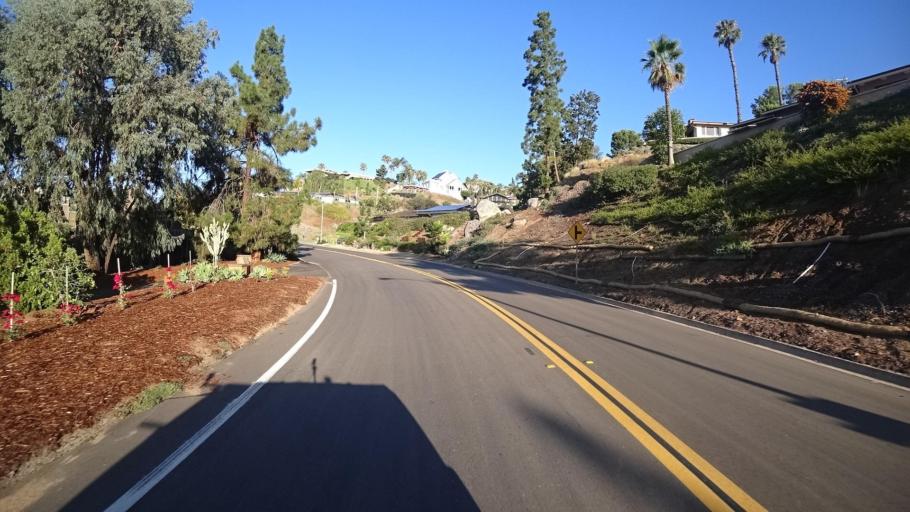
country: US
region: California
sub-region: San Diego County
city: Casa de Oro-Mount Helix
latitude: 32.7633
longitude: -116.9851
